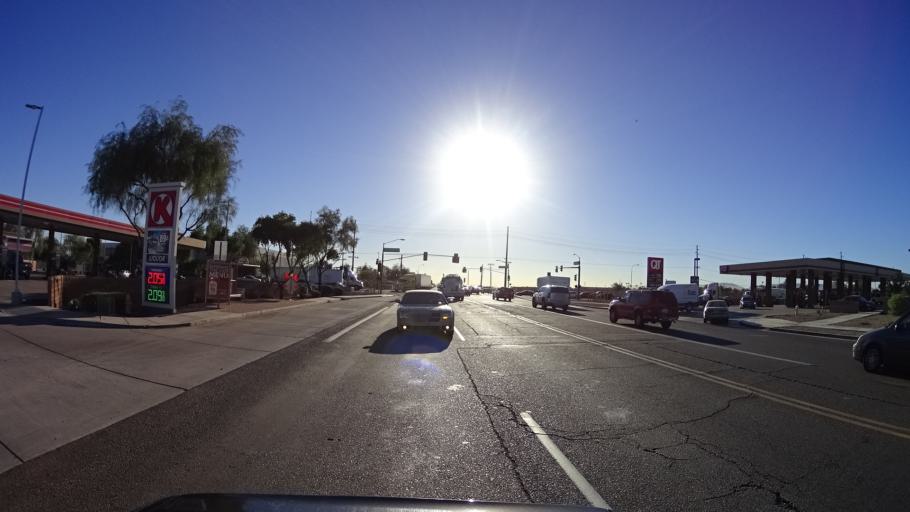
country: US
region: Arizona
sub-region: Maricopa County
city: Tolleson
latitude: 33.4373
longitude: -112.2045
